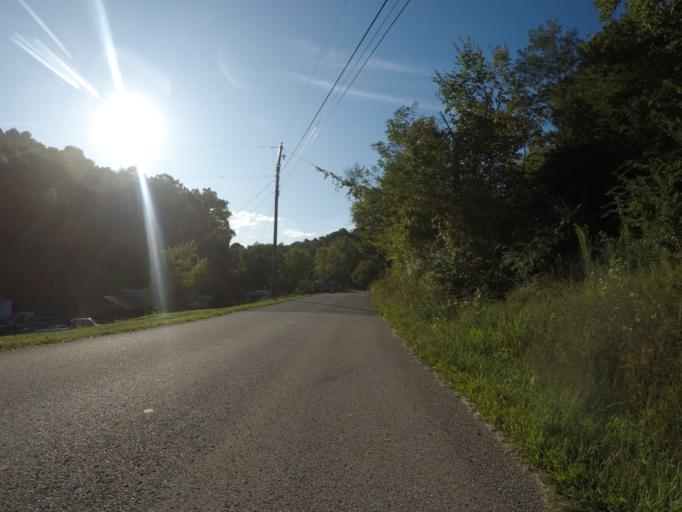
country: US
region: Ohio
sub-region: Lawrence County
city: Burlington
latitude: 38.5243
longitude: -82.5123
